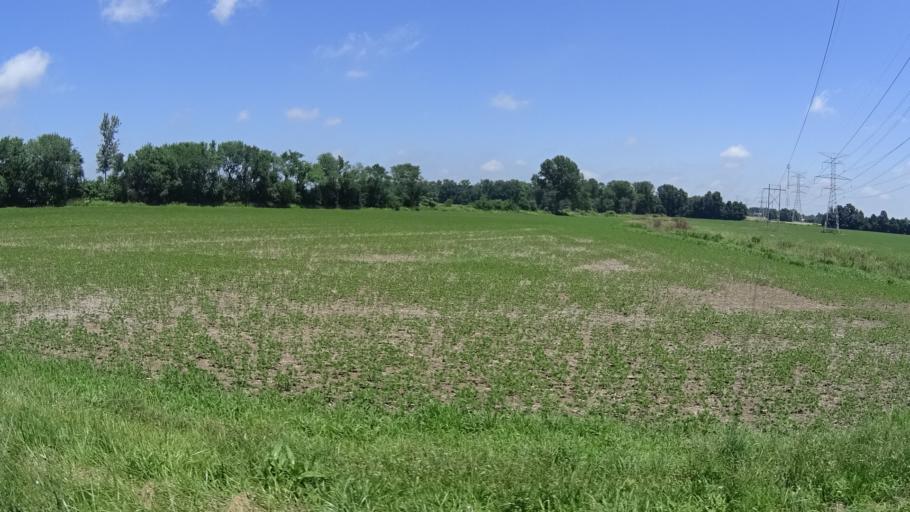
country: US
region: Ohio
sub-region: Huron County
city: Wakeman
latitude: 41.3377
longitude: -82.4199
